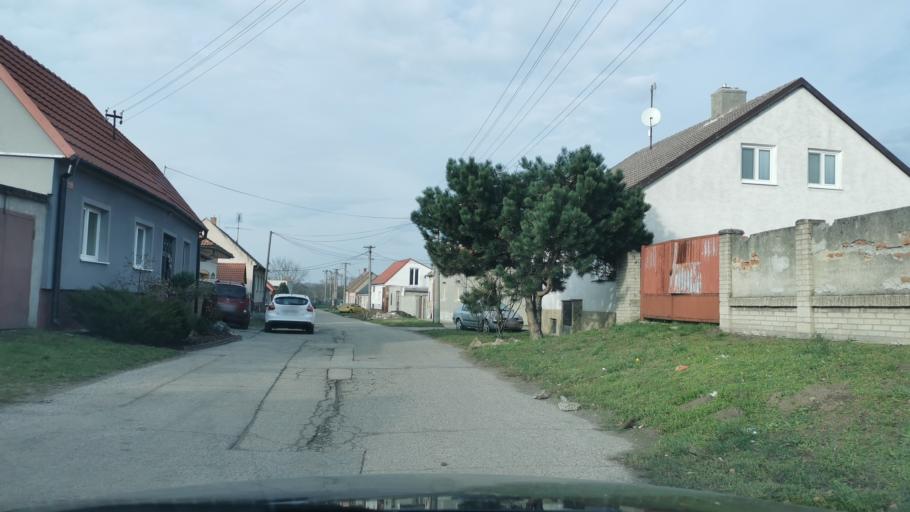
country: SK
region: Trnavsky
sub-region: Okres Skalica
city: Holic
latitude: 48.7875
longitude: 17.1090
